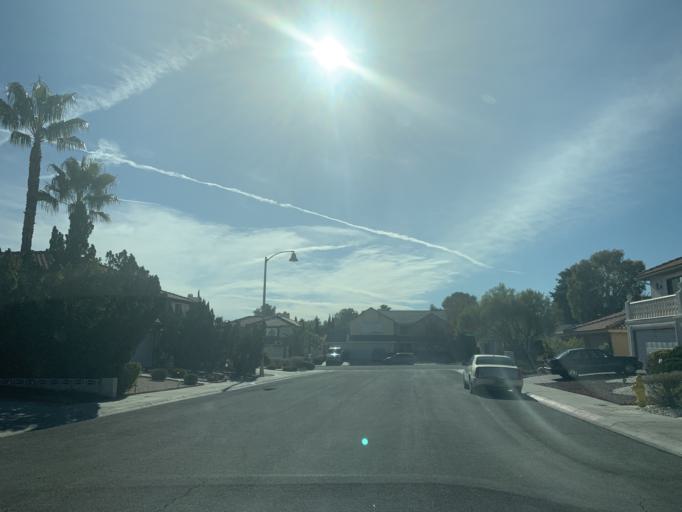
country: US
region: Nevada
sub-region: Clark County
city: Summerlin South
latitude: 36.1350
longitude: -115.2920
